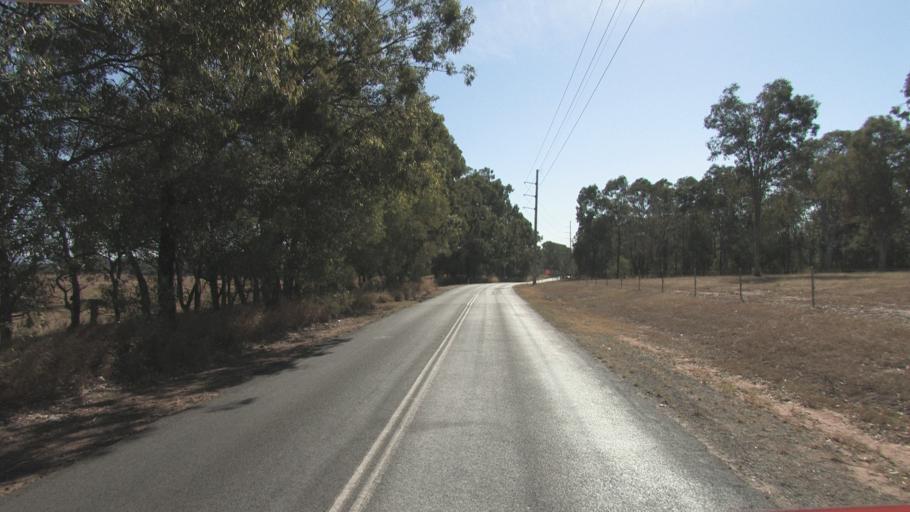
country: AU
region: Queensland
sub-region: Logan
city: Cedar Vale
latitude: -27.8653
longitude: 153.0177
